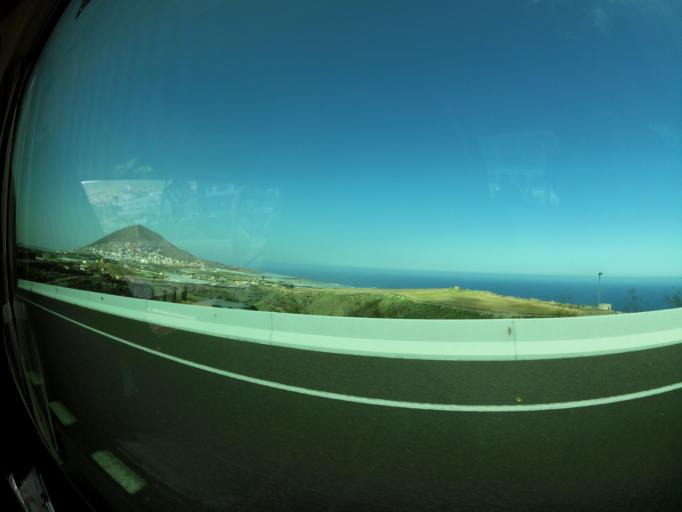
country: ES
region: Canary Islands
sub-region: Provincia de Las Palmas
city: Guia
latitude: 28.1446
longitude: -15.6144
